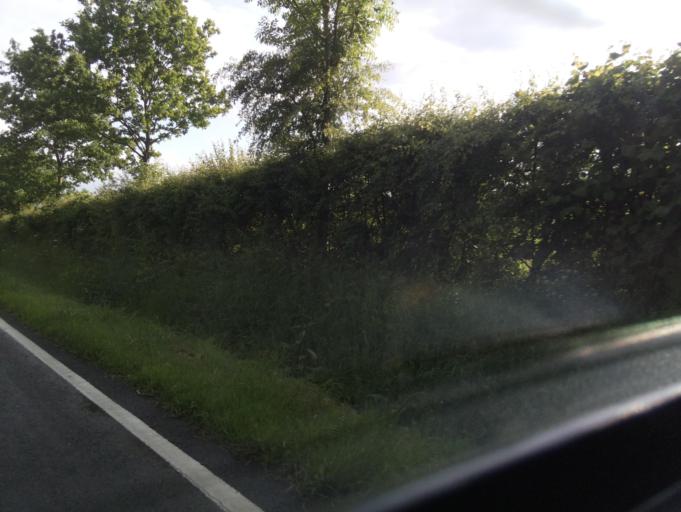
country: GB
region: England
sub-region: Lincolnshire
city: Navenby
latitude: 53.0583
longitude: -0.6411
